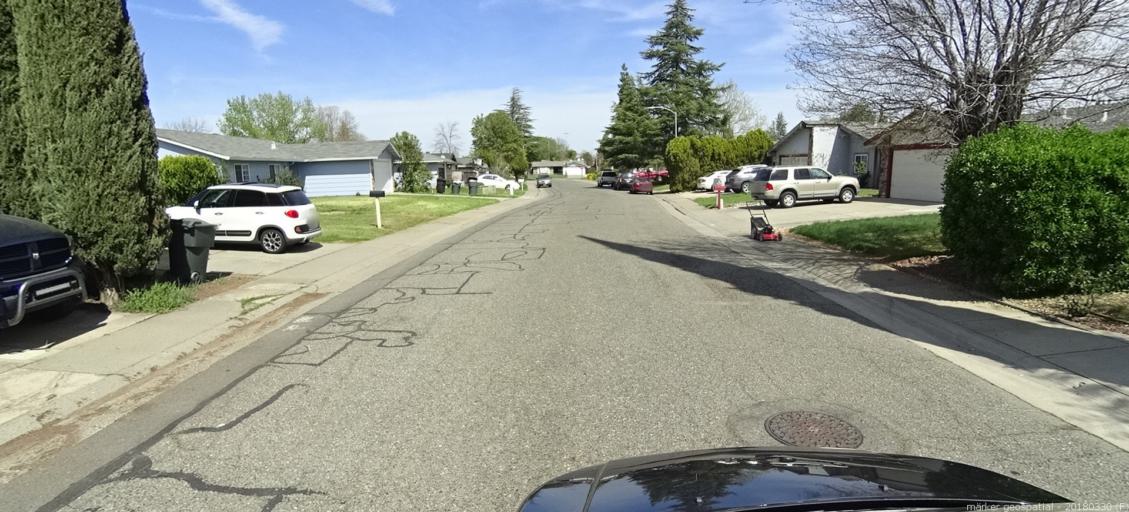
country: US
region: California
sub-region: Sacramento County
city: Rosemont
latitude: 38.5399
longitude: -121.3658
